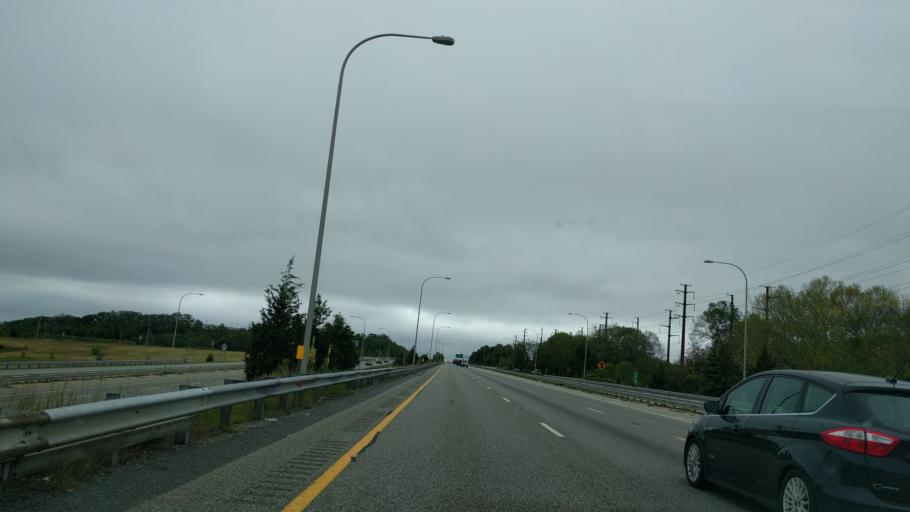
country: US
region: Rhode Island
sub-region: Providence County
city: Johnston
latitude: 41.8240
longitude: -71.5147
